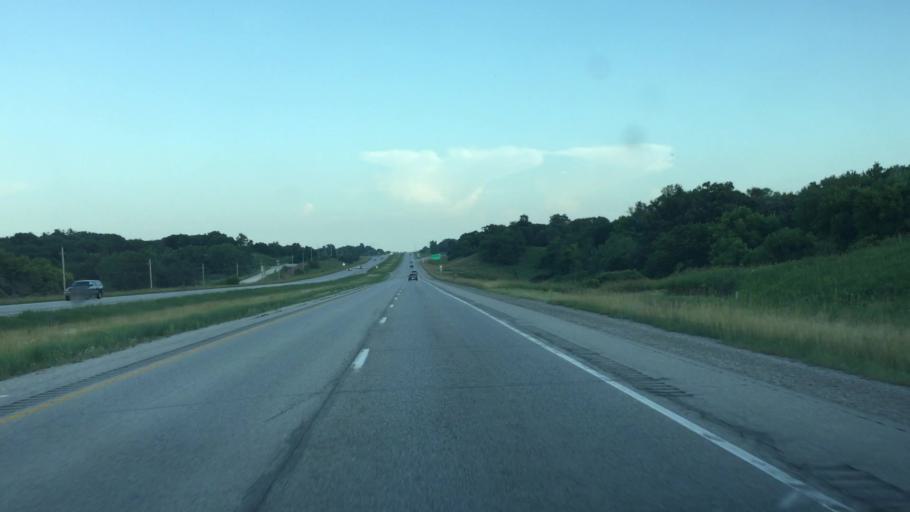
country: US
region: Iowa
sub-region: Johnson County
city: Coralville
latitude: 41.6654
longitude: -91.6097
